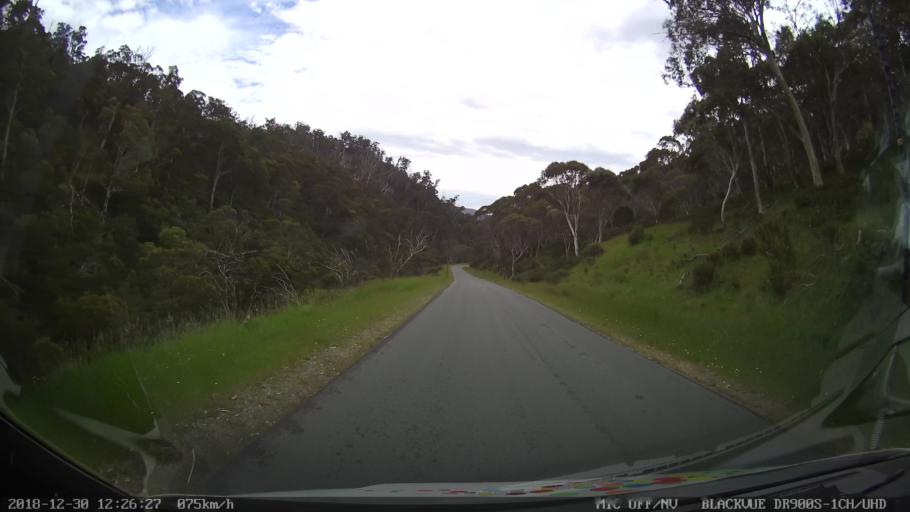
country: AU
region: New South Wales
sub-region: Snowy River
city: Jindabyne
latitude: -36.3390
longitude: 148.4893
